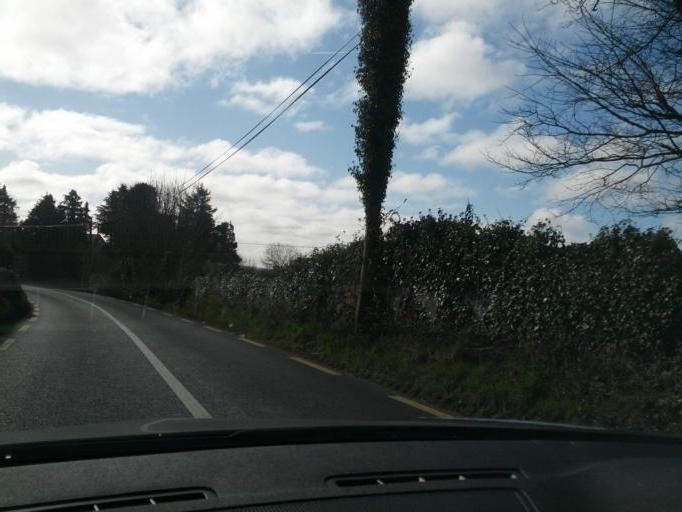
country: IE
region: Connaught
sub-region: County Galway
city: Ballinasloe
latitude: 53.3902
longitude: -8.3127
